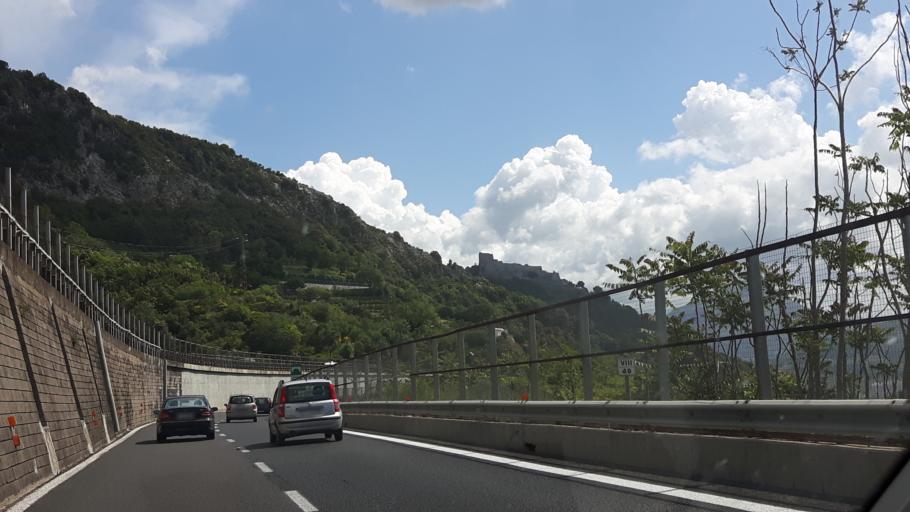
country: IT
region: Campania
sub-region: Provincia di Salerno
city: Vietri sul Mare
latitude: 40.6781
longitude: 14.7400
